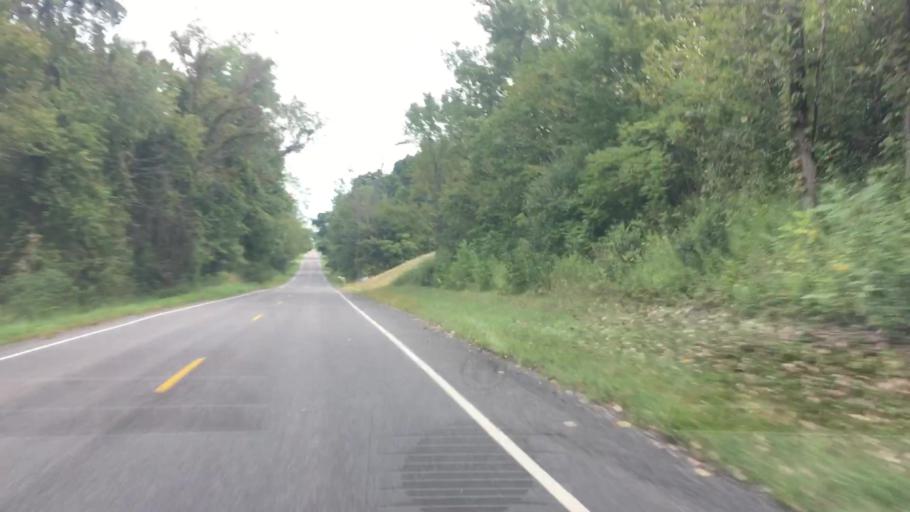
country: US
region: Michigan
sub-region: Kent County
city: Byron Center
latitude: 42.8342
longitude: -85.7826
